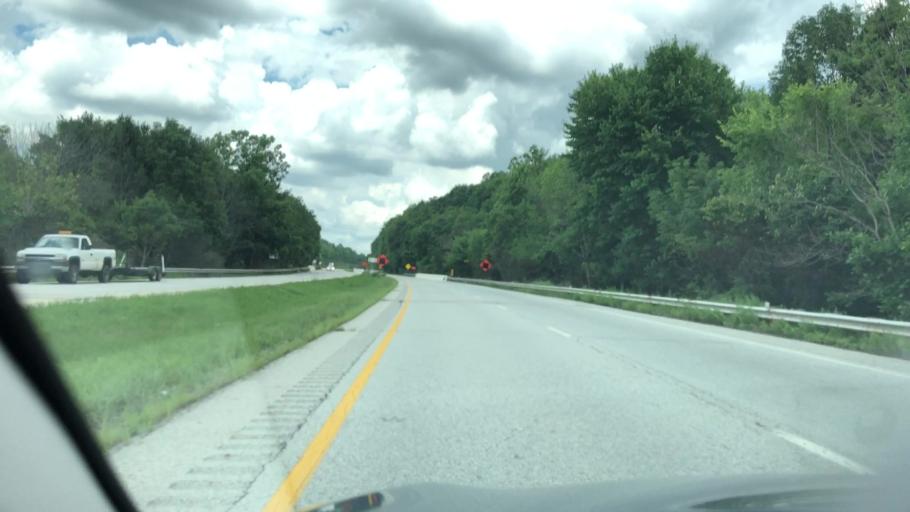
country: US
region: Ohio
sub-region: Summit County
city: Clinton
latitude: 40.9294
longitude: -81.6501
